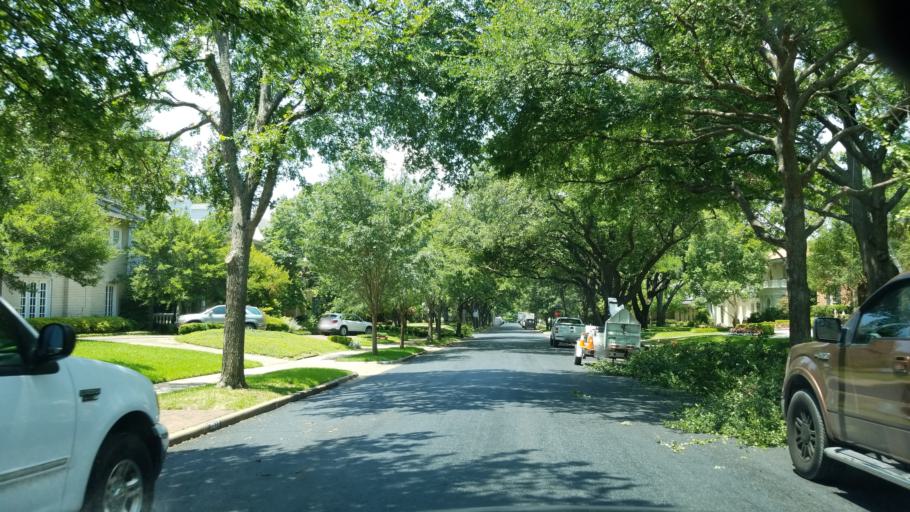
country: US
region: Texas
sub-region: Dallas County
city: Highland Park
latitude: 32.8312
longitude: -96.7900
